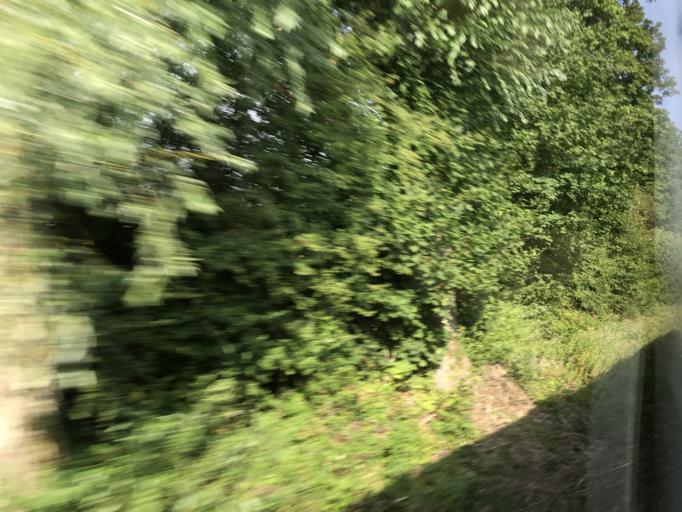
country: DE
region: Hesse
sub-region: Regierungsbezirk Darmstadt
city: Niedernhausen
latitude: 50.0979
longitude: 8.3196
